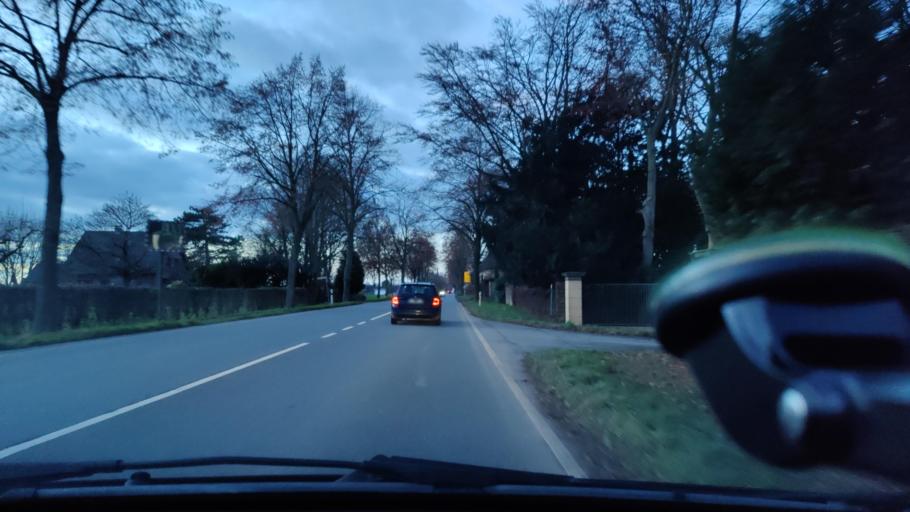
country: DE
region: North Rhine-Westphalia
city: Rees
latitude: 51.6920
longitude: 6.3879
